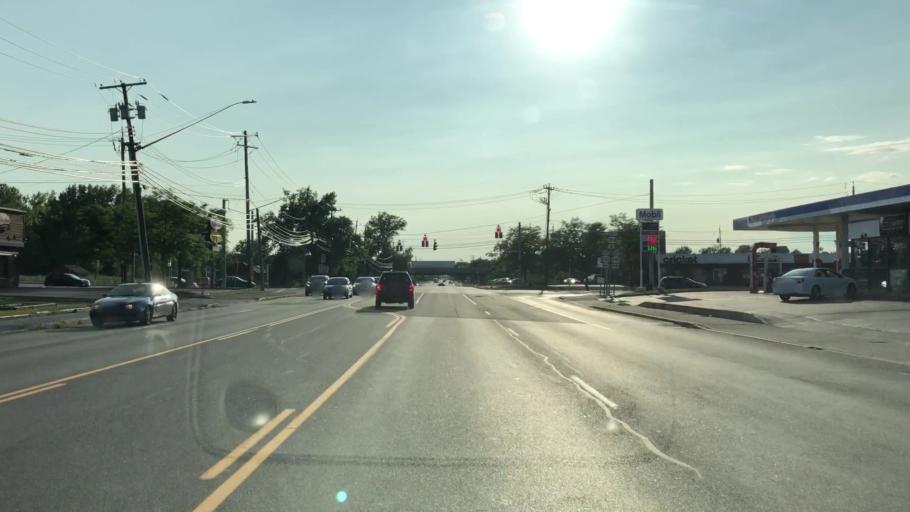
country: US
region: New York
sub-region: Erie County
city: Sloan
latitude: 42.8715
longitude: -78.7862
